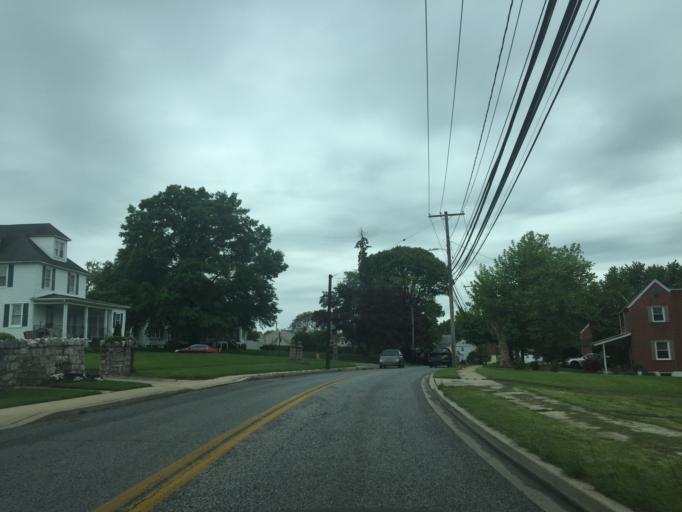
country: US
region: Maryland
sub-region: Baltimore County
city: Overlea
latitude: 39.3553
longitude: -76.5196
